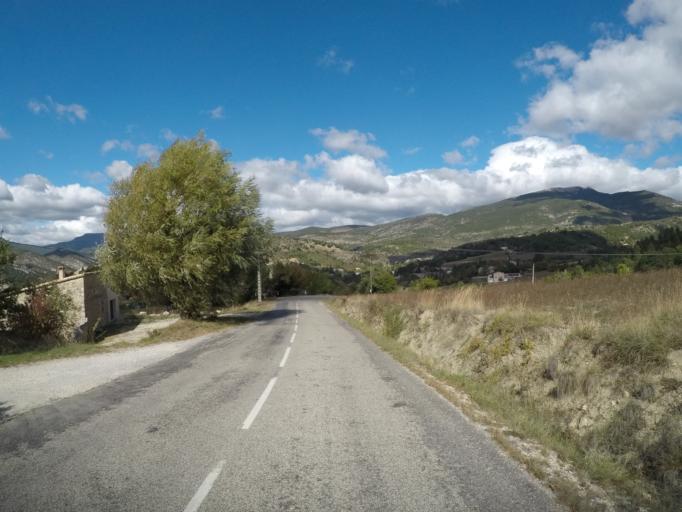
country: FR
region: Provence-Alpes-Cote d'Azur
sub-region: Departement du Vaucluse
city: Sault
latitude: 44.1674
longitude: 5.4476
